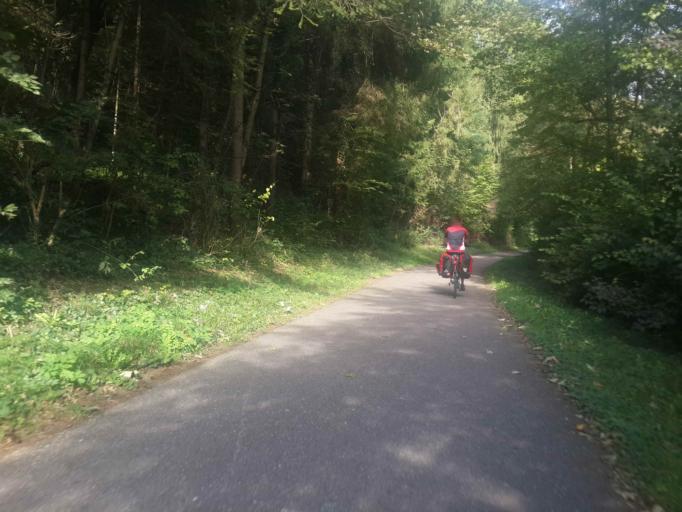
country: DE
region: Baden-Wuerttemberg
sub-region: Regierungsbezirk Stuttgart
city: Neudenau
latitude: 49.2890
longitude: 9.2537
